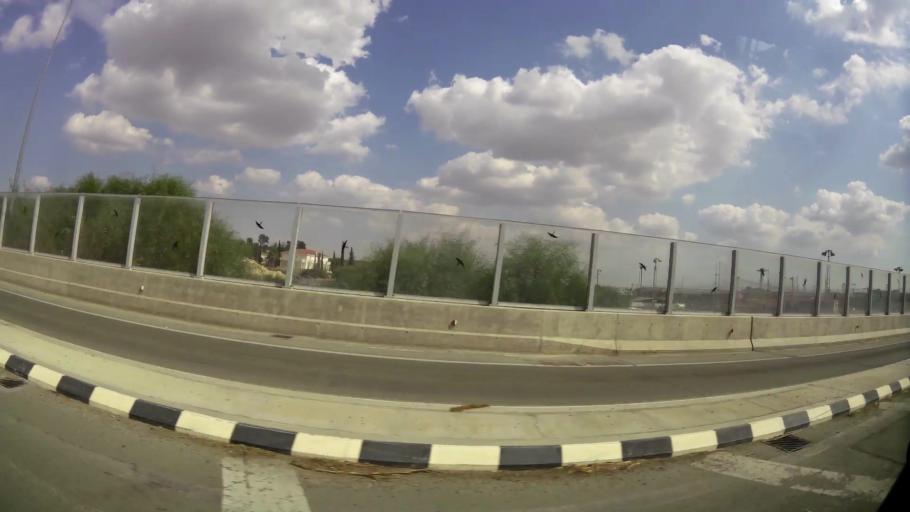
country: CY
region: Lefkosia
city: Geri
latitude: 35.1174
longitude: 33.3636
